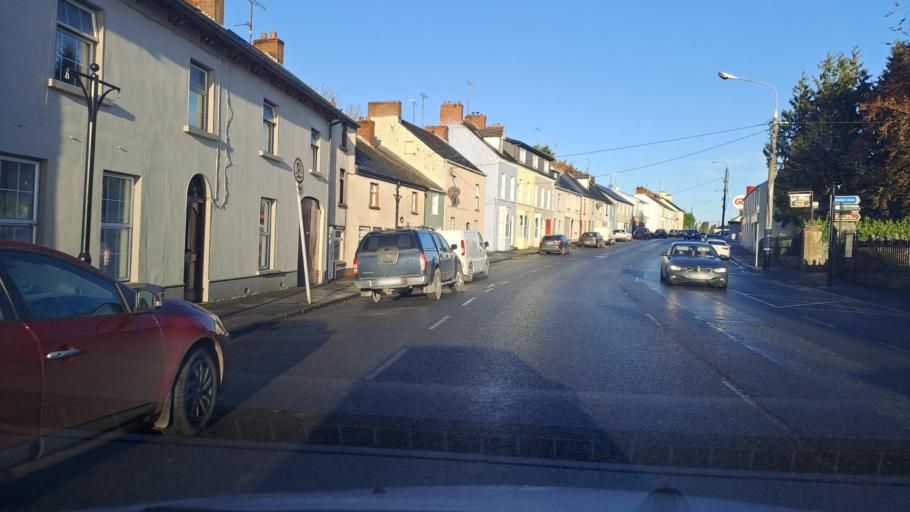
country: IE
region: Ulster
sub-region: An Cabhan
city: Cootehill
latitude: 54.0734
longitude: -7.0843
